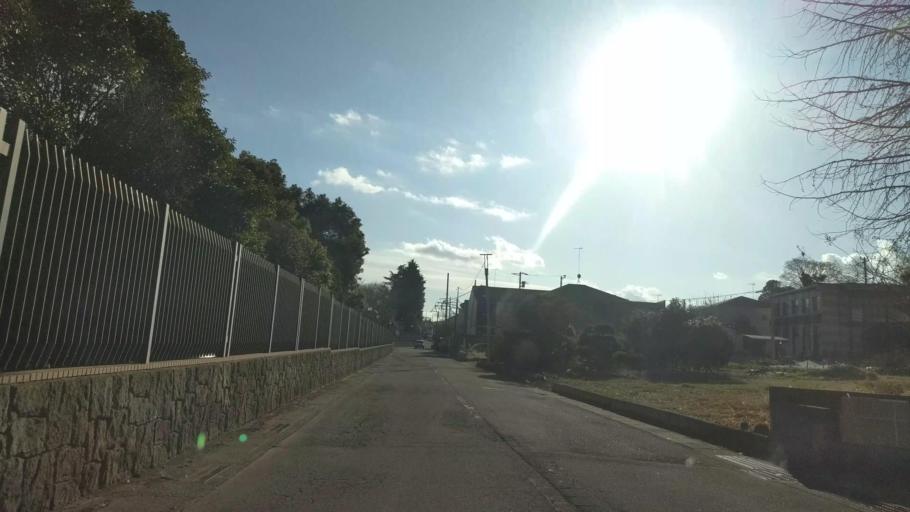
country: JP
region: Kanagawa
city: Isehara
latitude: 35.3639
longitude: 139.2717
